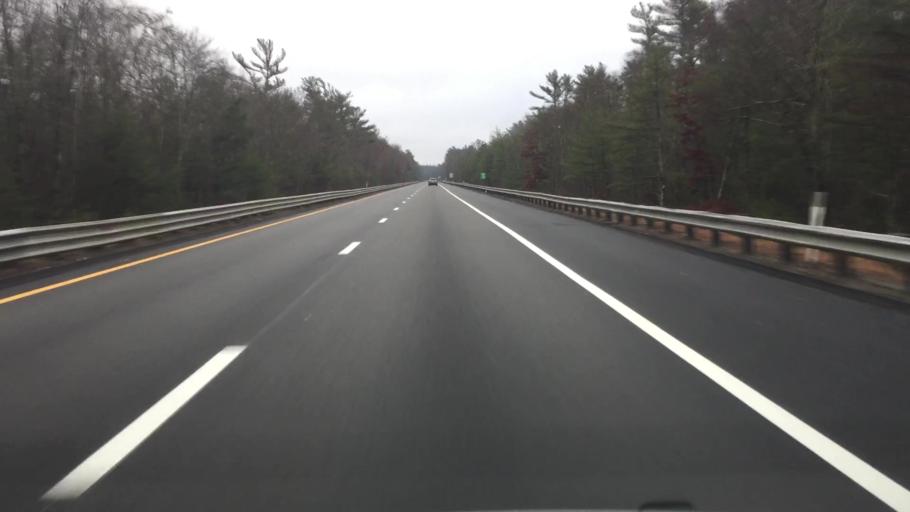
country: US
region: Massachusetts
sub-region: Plymouth County
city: West Wareham
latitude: 41.8238
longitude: -70.8079
